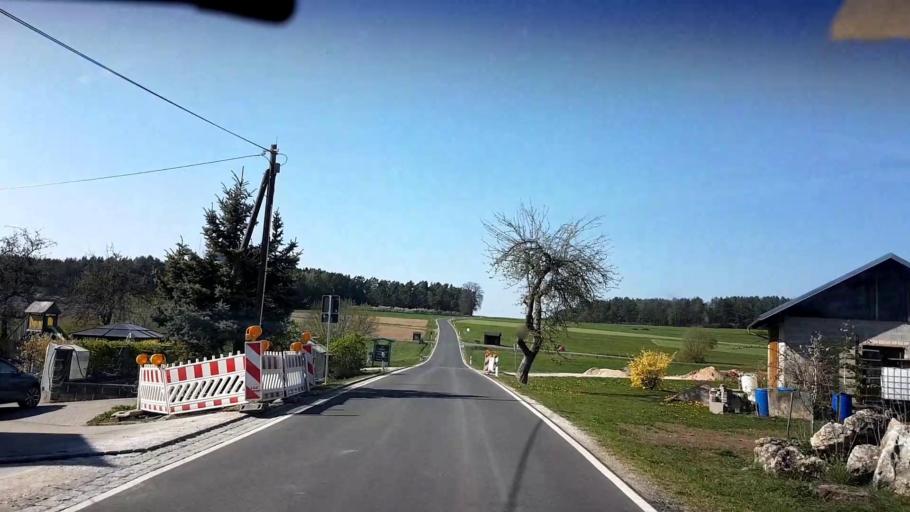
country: DE
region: Bavaria
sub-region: Upper Franconia
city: Pottenstein
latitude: 49.7984
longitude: 11.3766
